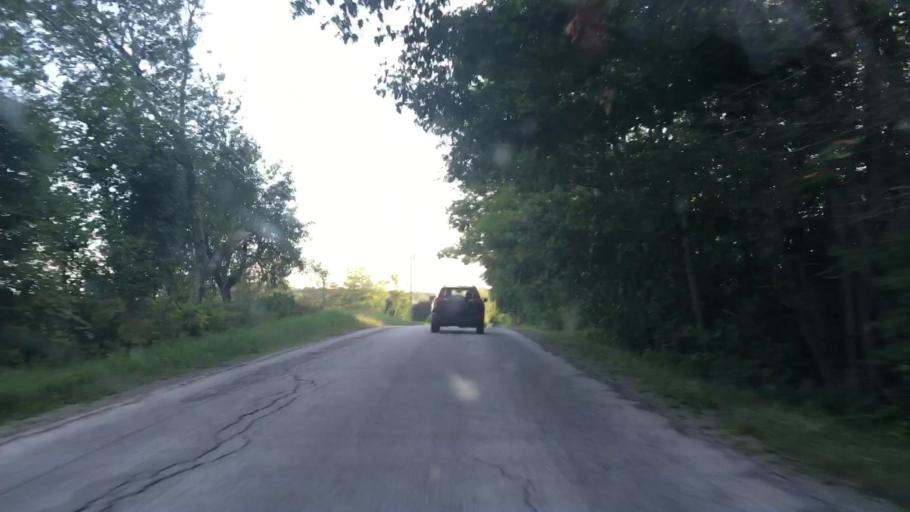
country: US
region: Maine
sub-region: Waldo County
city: Frankfort
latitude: 44.6780
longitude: -68.9158
